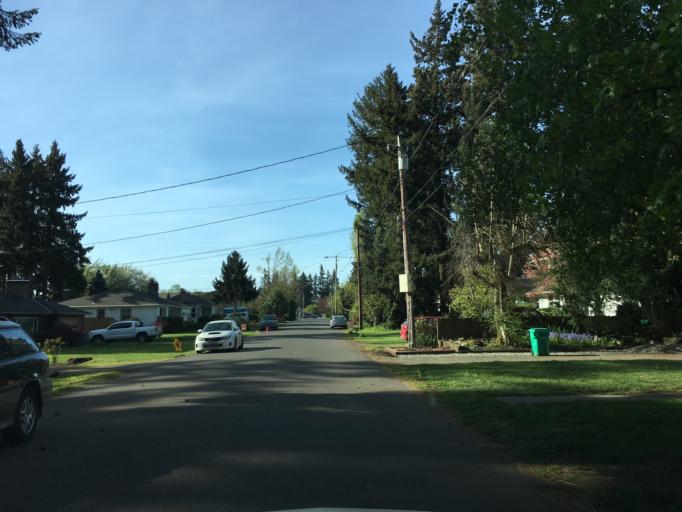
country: US
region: Oregon
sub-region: Multnomah County
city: Lents
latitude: 45.5360
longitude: -122.5535
